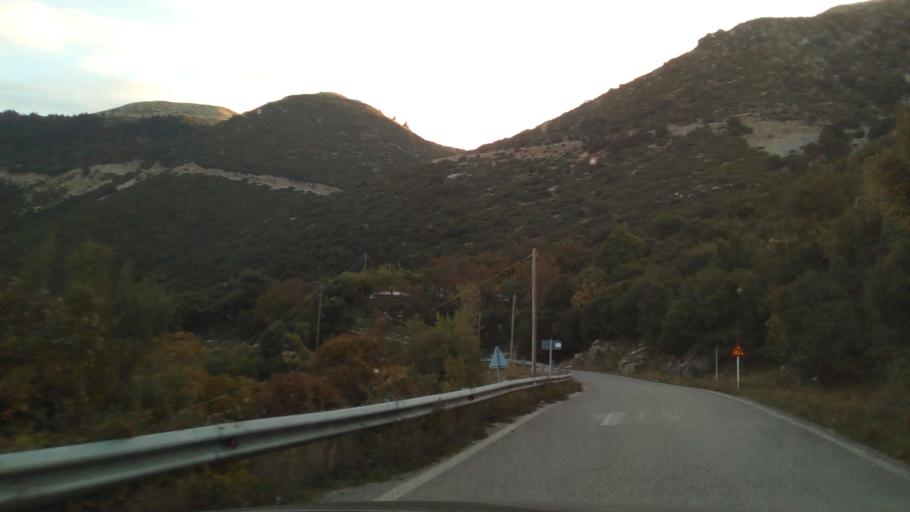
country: GR
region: West Greece
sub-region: Nomos Aitolias kai Akarnanias
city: Nafpaktos
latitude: 38.5145
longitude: 21.8420
